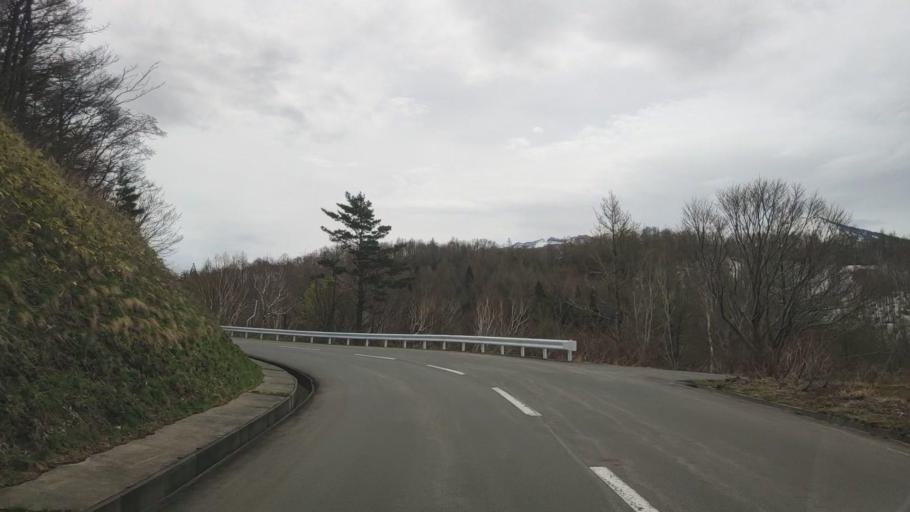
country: JP
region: Aomori
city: Aomori Shi
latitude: 40.7147
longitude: 140.8712
